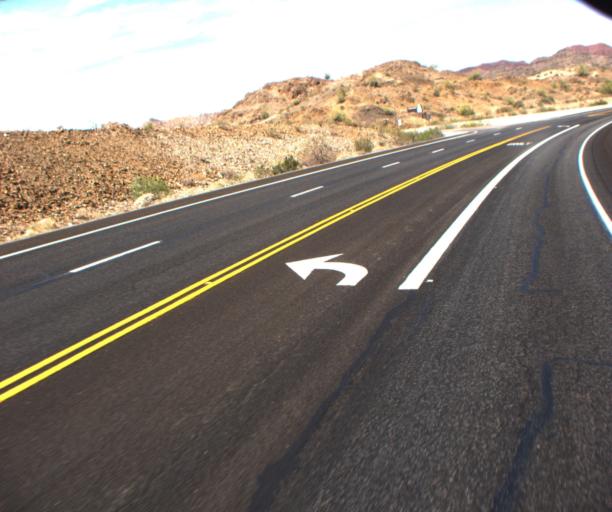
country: US
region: Arizona
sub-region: La Paz County
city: Cienega Springs
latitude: 34.2535
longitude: -114.1614
